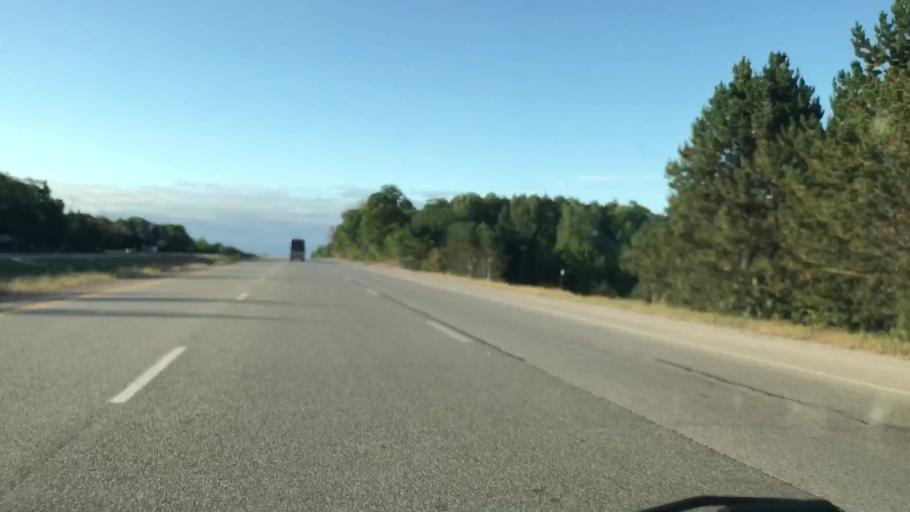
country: US
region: Michigan
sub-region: Chippewa County
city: Sault Ste. Marie
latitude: 46.4615
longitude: -84.3836
